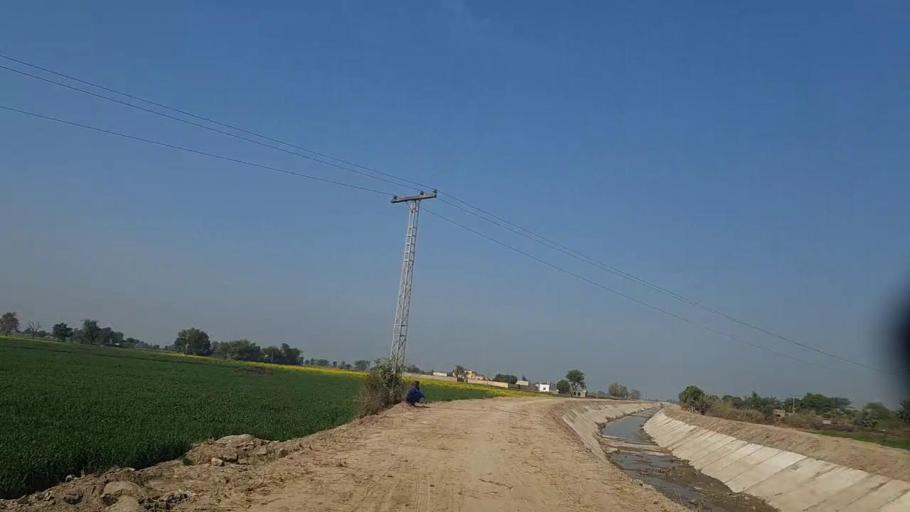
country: PK
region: Sindh
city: Sakrand
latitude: 26.1477
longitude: 68.3327
